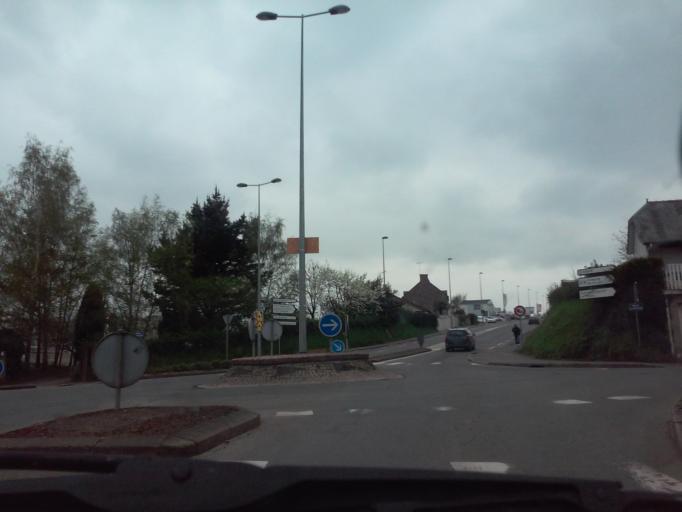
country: FR
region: Brittany
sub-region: Departement d'Ille-et-Vilaine
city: Fougeres
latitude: 48.3525
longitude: -1.1859
